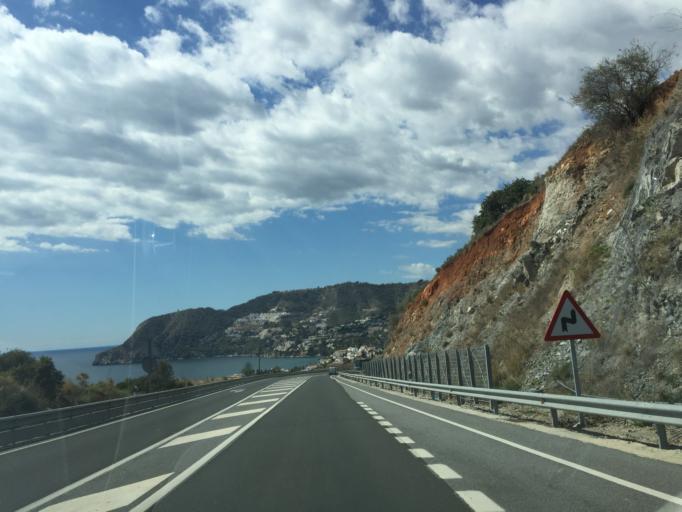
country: ES
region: Andalusia
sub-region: Provincia de Granada
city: La Herradura
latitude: 36.7369
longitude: -3.7320
